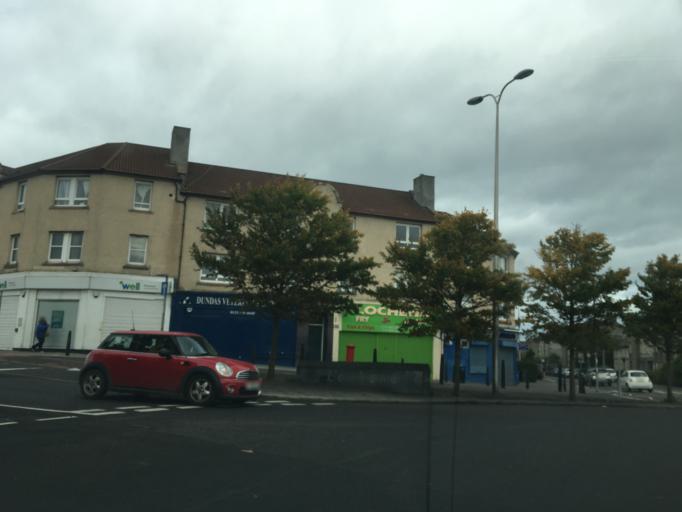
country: GB
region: Scotland
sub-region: West Lothian
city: Seafield
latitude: 55.9591
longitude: -3.1564
